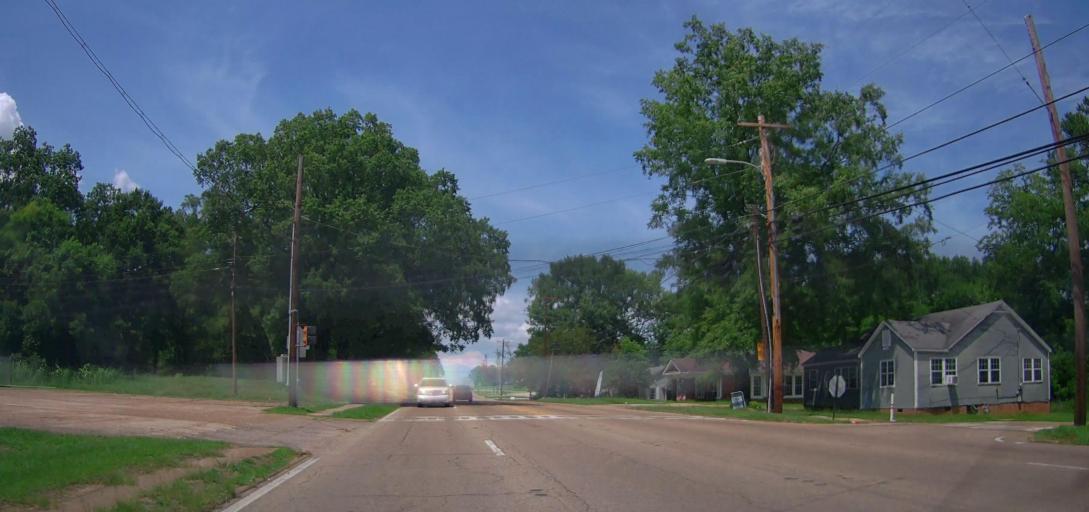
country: US
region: Mississippi
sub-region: Lee County
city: Verona
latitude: 34.2010
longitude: -88.7201
